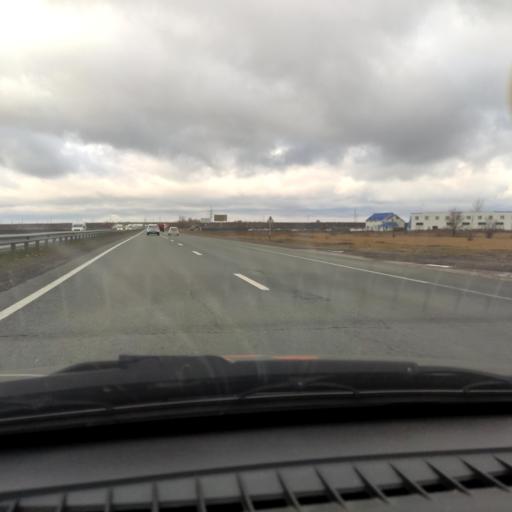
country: RU
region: Samara
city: Zhigulevsk
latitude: 53.5574
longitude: 49.5018
